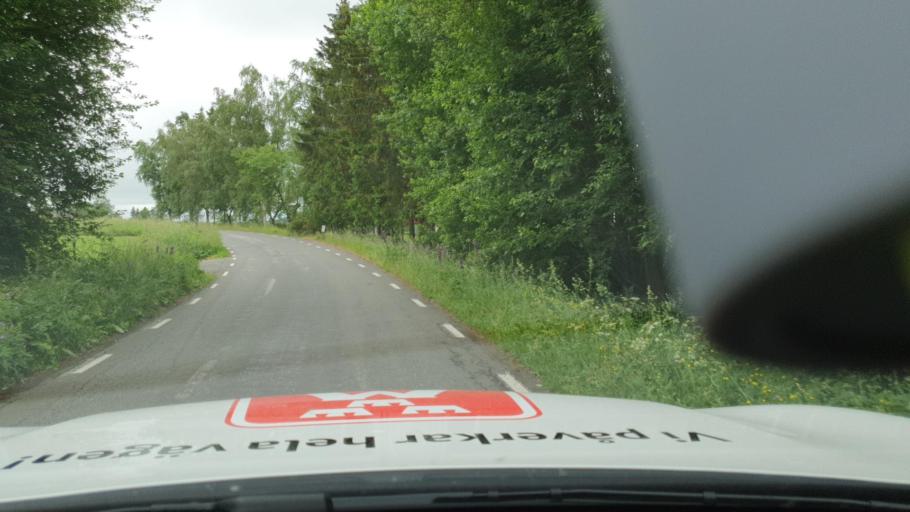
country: SE
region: Vaestra Goetaland
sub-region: Tidaholms Kommun
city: Olofstorp
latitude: 58.3776
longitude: 14.0032
